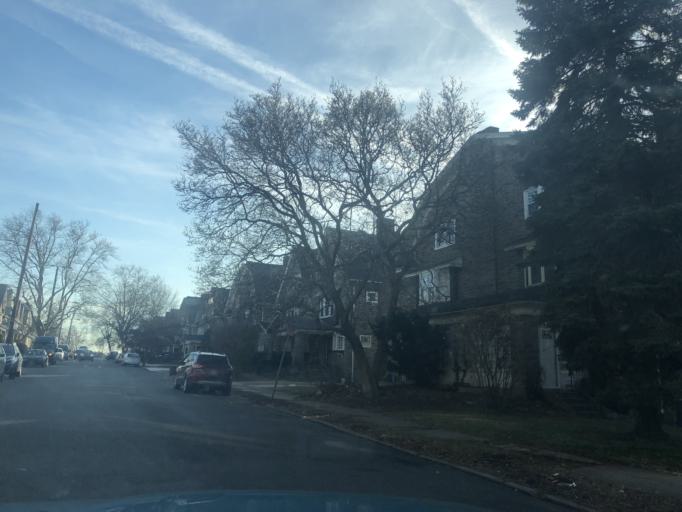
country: US
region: Pennsylvania
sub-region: Delaware County
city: Millbourne
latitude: 39.9780
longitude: -75.2483
